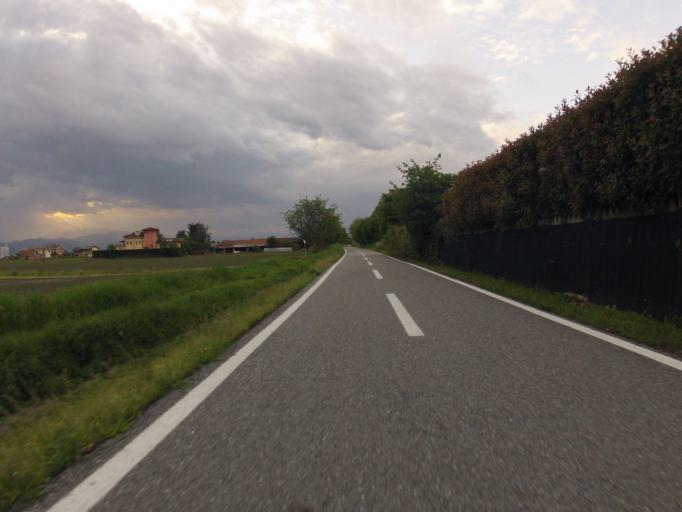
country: IT
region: Piedmont
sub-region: Provincia di Torino
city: Vigone
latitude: 44.8373
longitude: 7.4914
